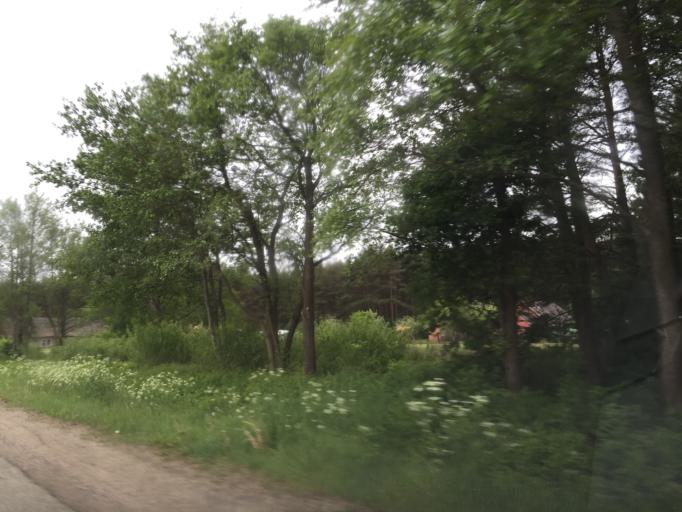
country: LT
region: Klaipedos apskritis
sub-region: Klaipeda
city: Palanga
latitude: 55.8134
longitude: 21.0710
